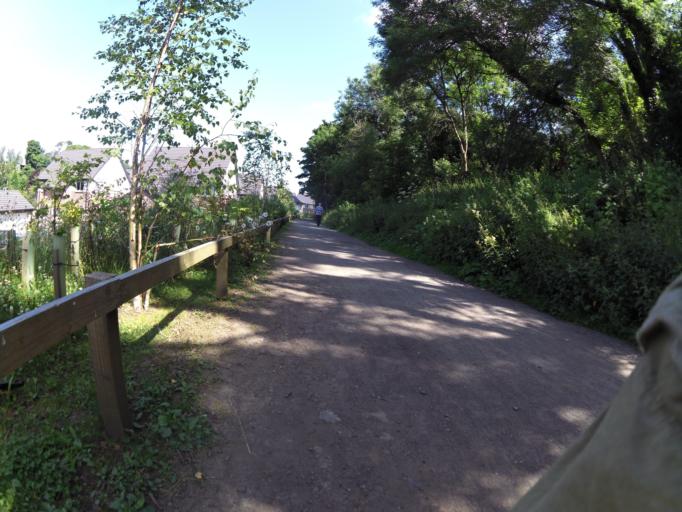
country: GB
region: Scotland
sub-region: Edinburgh
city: Currie
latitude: 55.8971
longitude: -3.3015
